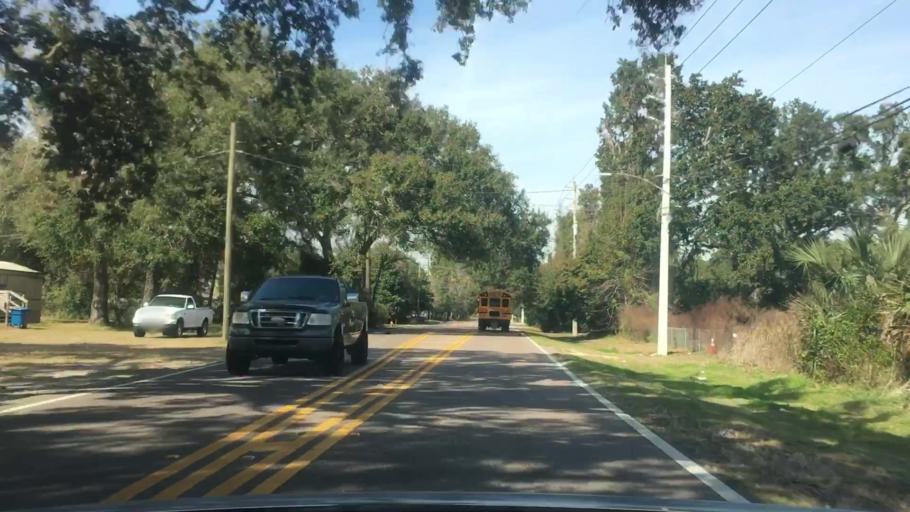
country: US
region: Florida
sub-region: Duval County
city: Jacksonville
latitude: 30.4595
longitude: -81.5598
